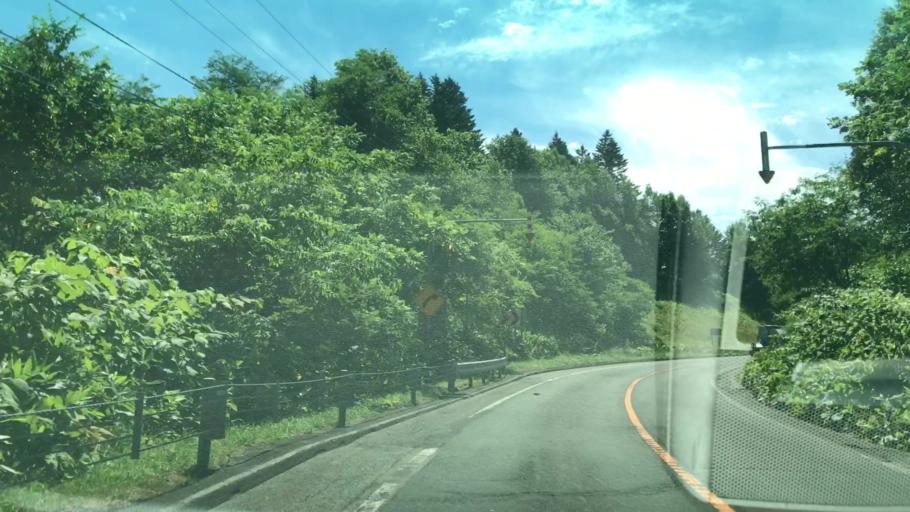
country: JP
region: Hokkaido
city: Shimo-furano
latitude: 42.9202
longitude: 142.4471
